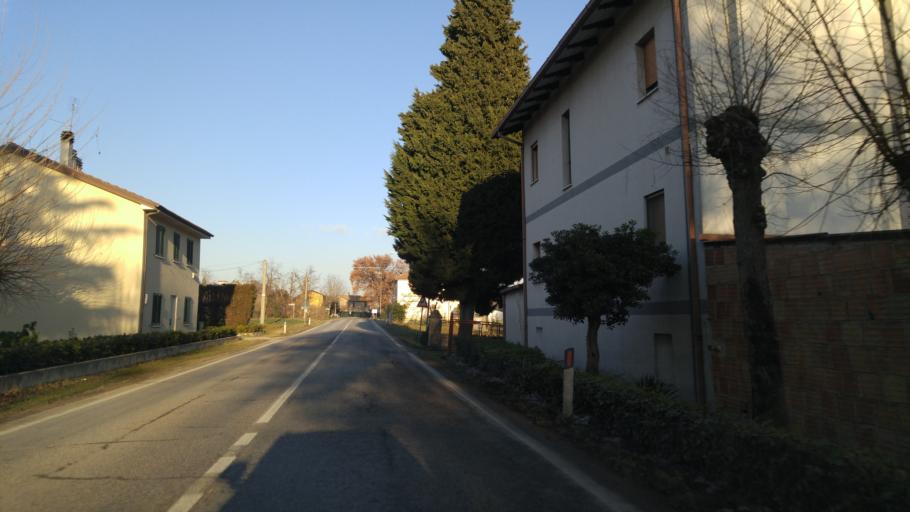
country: IT
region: The Marches
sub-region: Provincia di Pesaro e Urbino
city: San Michele
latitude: 43.6651
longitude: 13.0036
